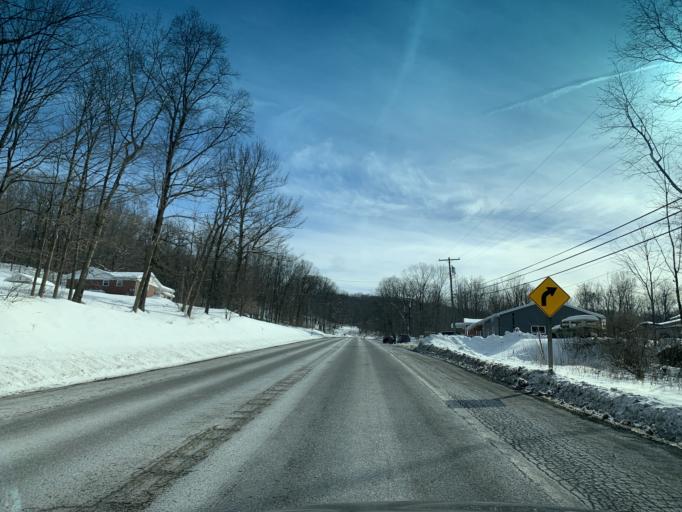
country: US
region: Maryland
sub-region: Allegany County
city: Frostburg
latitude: 39.6244
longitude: -78.8993
